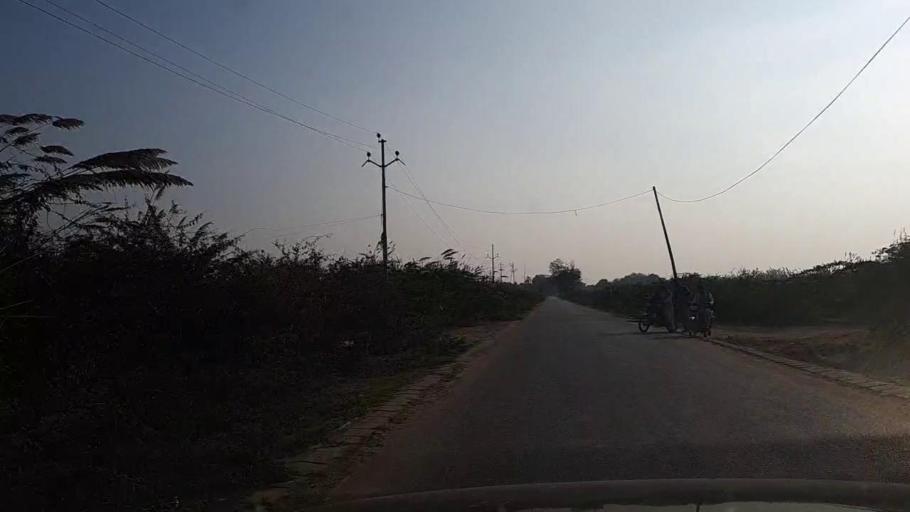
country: PK
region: Sindh
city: Gharo
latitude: 24.7822
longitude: 67.5119
